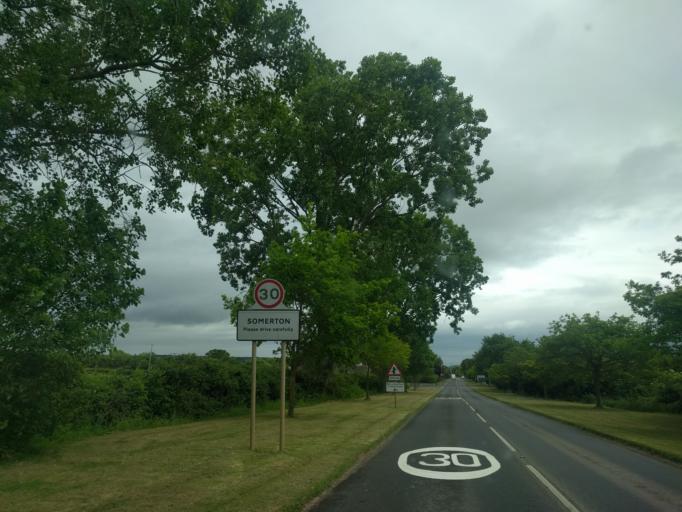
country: GB
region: England
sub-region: Somerset
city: Street
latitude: 51.0529
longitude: -2.7543
